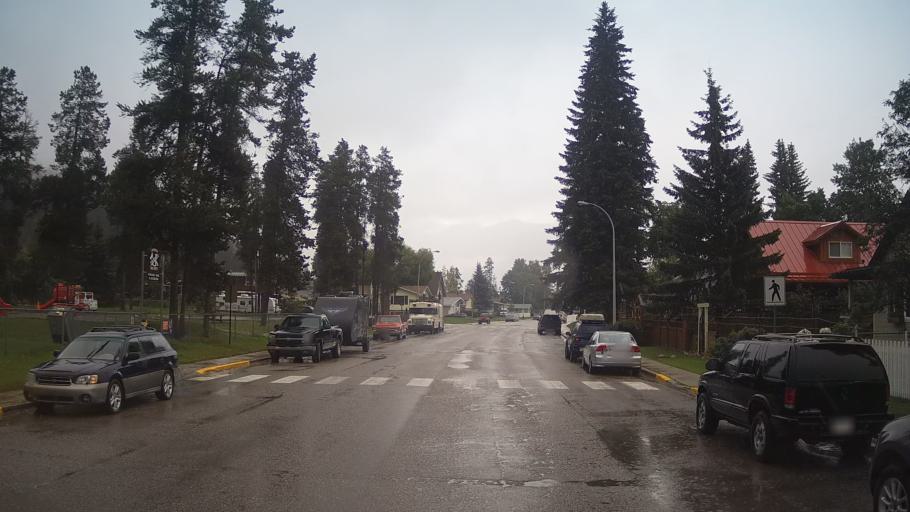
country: CA
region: Alberta
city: Jasper Park Lodge
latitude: 52.8818
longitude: -118.0846
